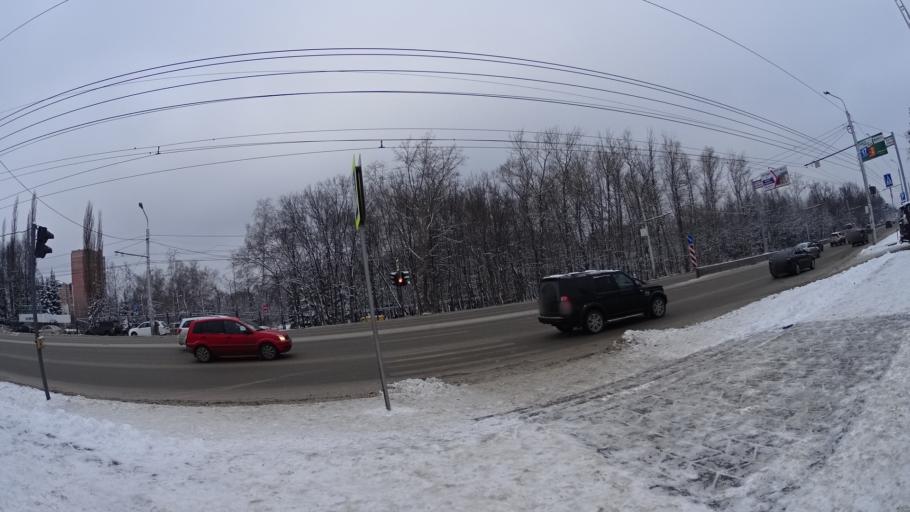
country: RU
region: Bashkortostan
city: Ufa
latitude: 54.7251
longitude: 56.0185
